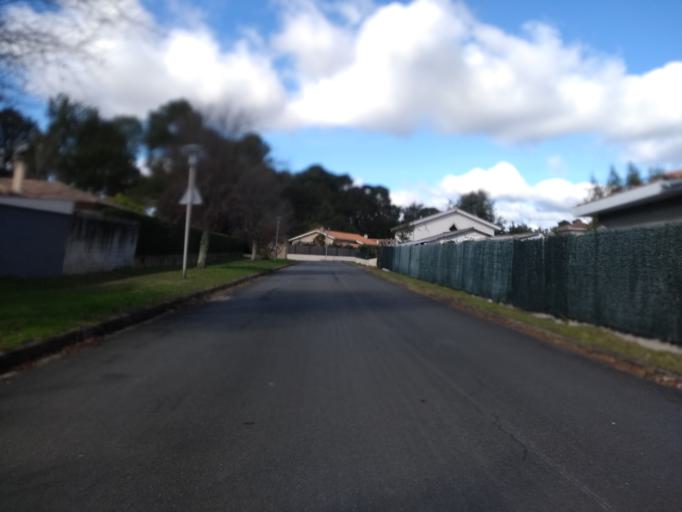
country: FR
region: Aquitaine
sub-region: Departement de la Gironde
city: Pessac
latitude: 44.8189
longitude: -0.6792
